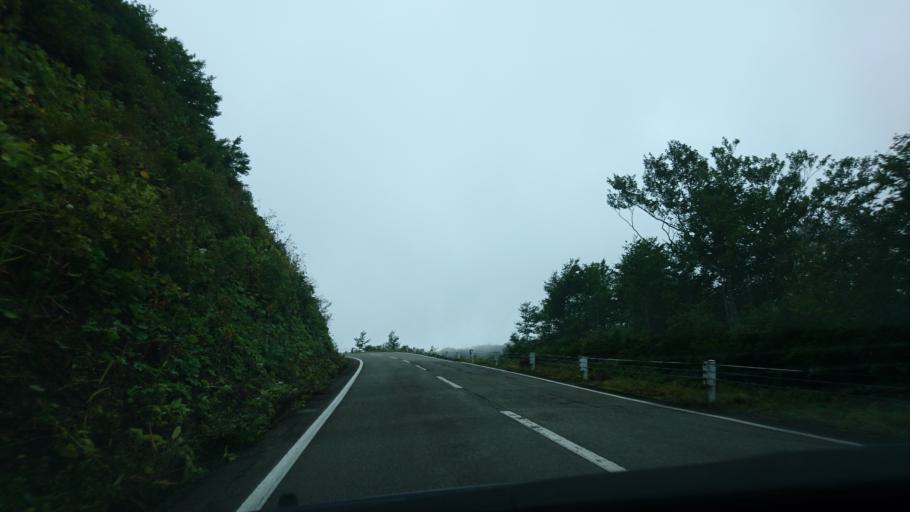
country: JP
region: Akita
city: Yuzawa
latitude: 38.9792
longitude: 140.7554
